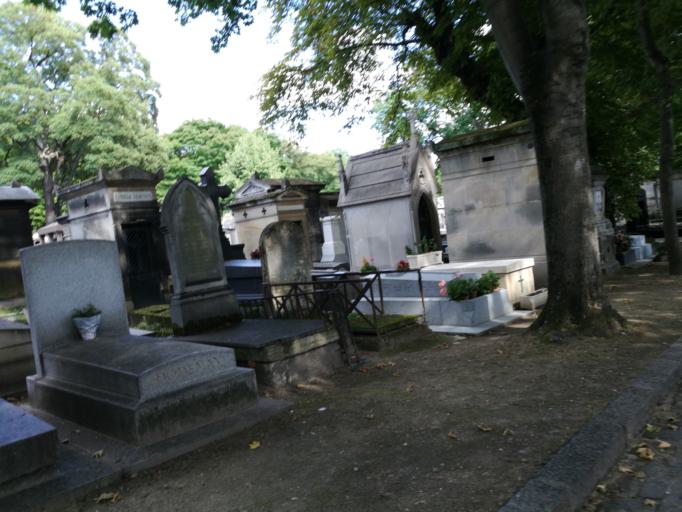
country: FR
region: Ile-de-France
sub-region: Paris
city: Saint-Ouen
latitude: 48.8865
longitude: 2.3296
